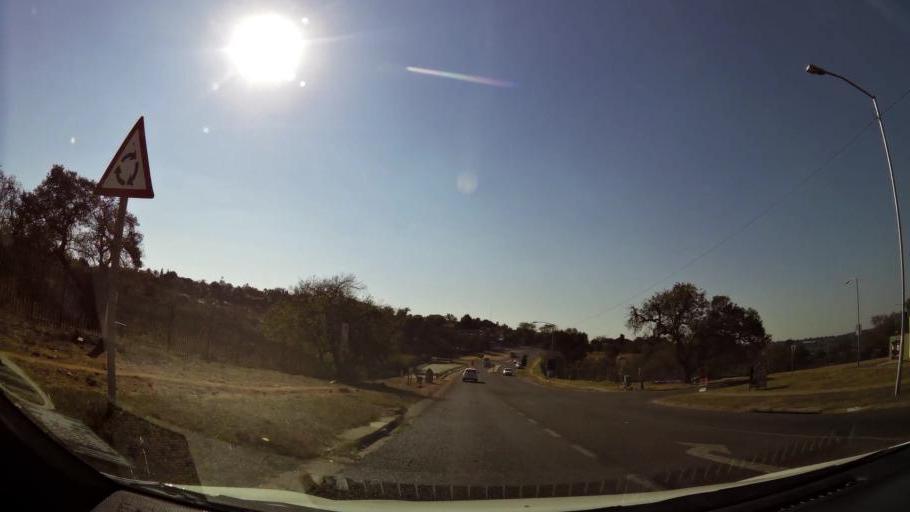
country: ZA
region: Gauteng
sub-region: City of Tshwane Metropolitan Municipality
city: Centurion
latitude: -25.8132
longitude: 28.2956
